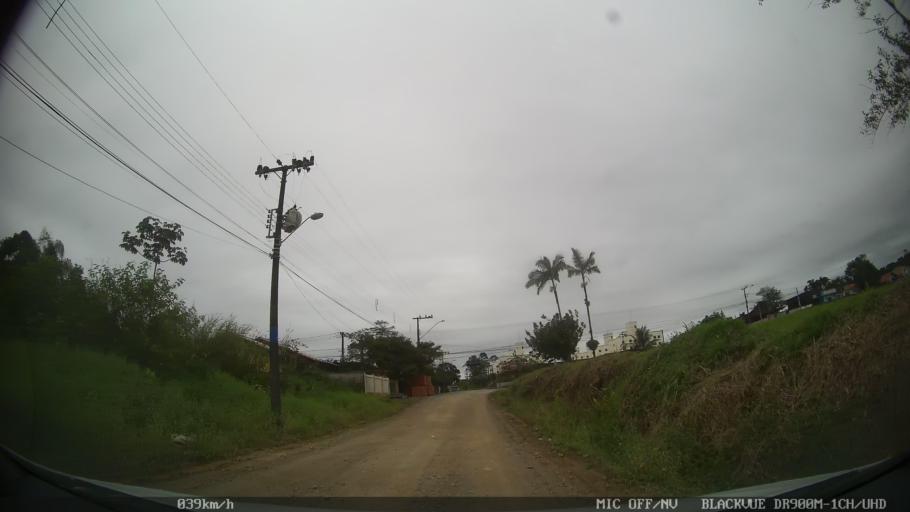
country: BR
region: Santa Catarina
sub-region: Joinville
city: Joinville
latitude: -26.2770
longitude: -48.9091
